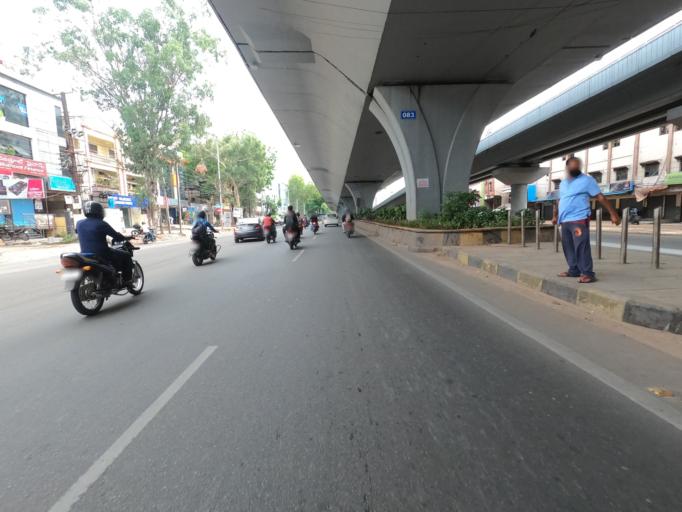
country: IN
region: Telangana
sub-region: Hyderabad
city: Hyderabad
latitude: 17.3827
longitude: 78.4294
